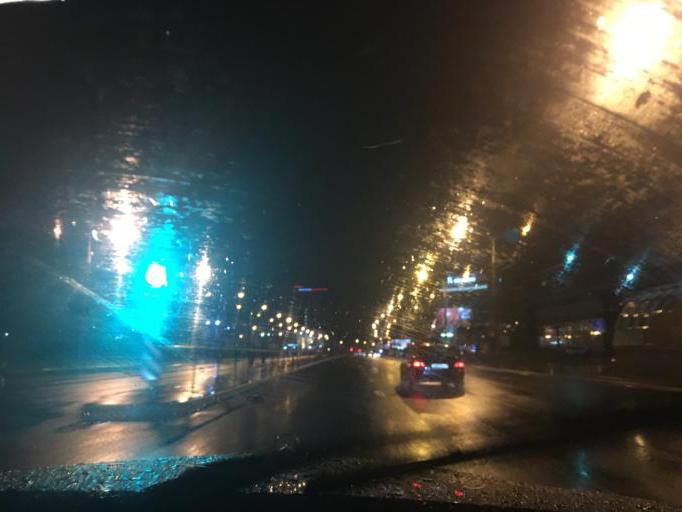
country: BY
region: Minsk
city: Minsk
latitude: 53.8908
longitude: 27.5246
